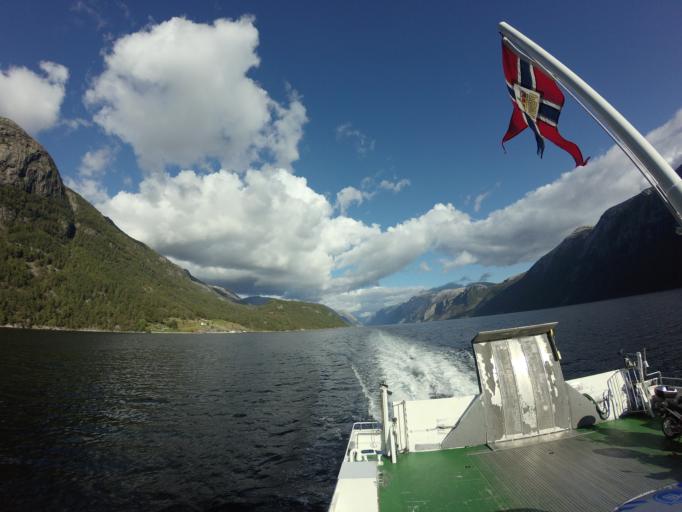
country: NO
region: Rogaland
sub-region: Forsand
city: Forsand
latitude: 59.0124
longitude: 6.3137
